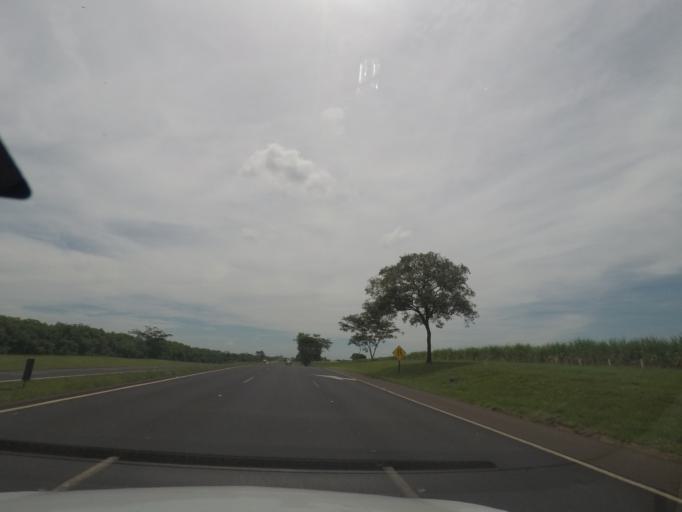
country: BR
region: Sao Paulo
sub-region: Bebedouro
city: Bebedouro
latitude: -20.9885
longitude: -48.4343
